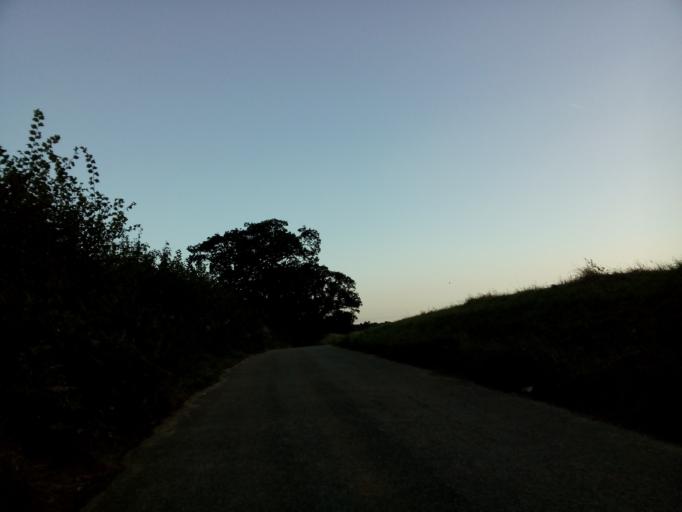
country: GB
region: England
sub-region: Suffolk
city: Bramford
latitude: 52.0551
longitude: 1.1058
